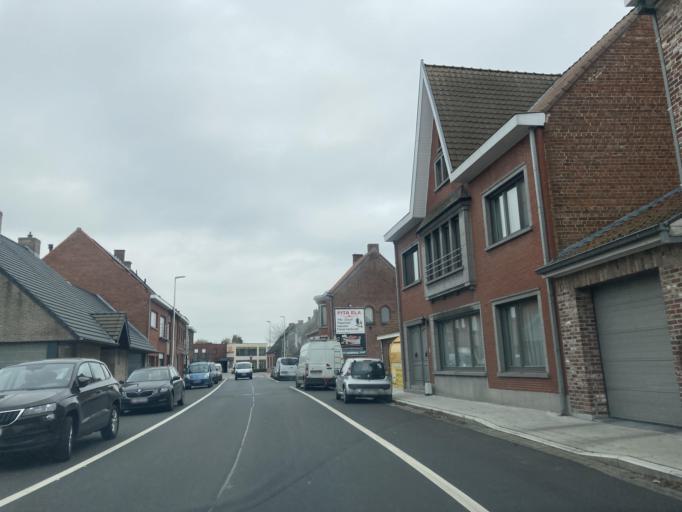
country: BE
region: Flanders
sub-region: Provincie West-Vlaanderen
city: Izegem
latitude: 50.8732
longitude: 3.1818
